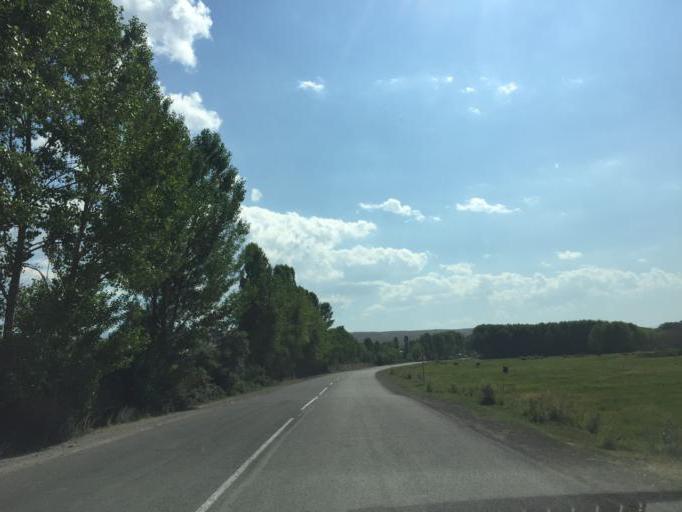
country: AM
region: Geghark'unik'i Marz
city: Artsvanist
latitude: 40.1617
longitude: 45.5030
